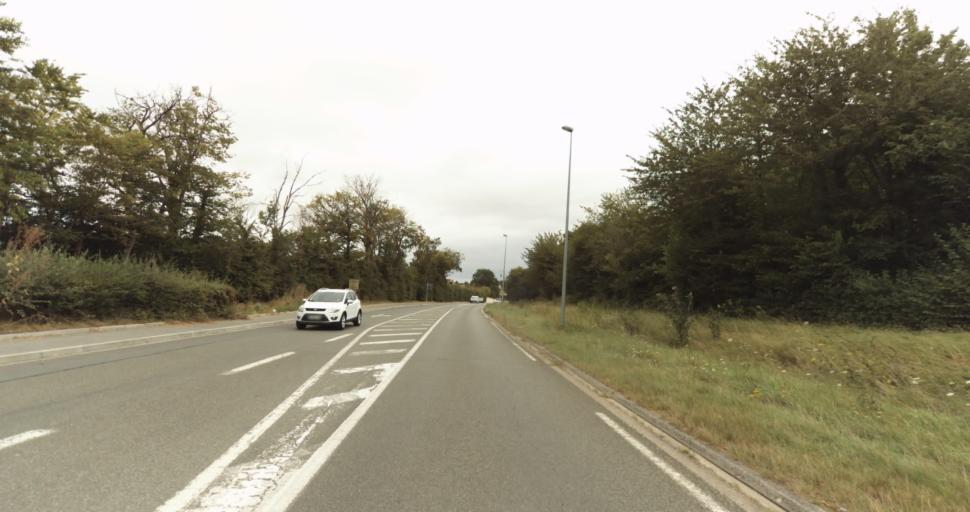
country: FR
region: Haute-Normandie
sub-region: Departement de l'Eure
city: Gravigny
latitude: 49.0295
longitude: 1.1902
